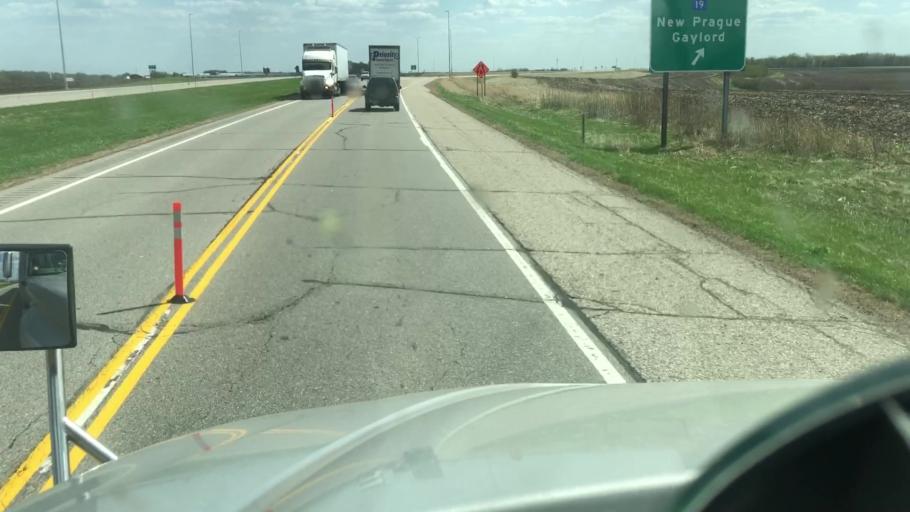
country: US
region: Minnesota
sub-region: Scott County
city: Belle Plaine
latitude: 44.5501
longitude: -93.8496
